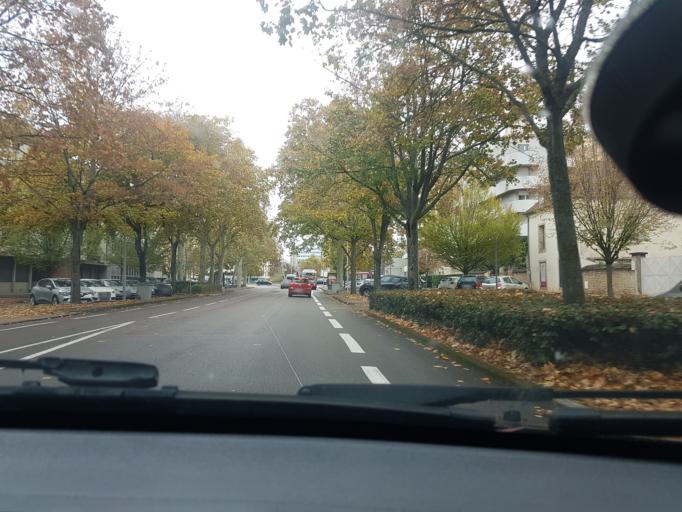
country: FR
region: Bourgogne
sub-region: Departement de la Cote-d'Or
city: Saint-Apollinaire
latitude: 47.3201
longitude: 5.0519
